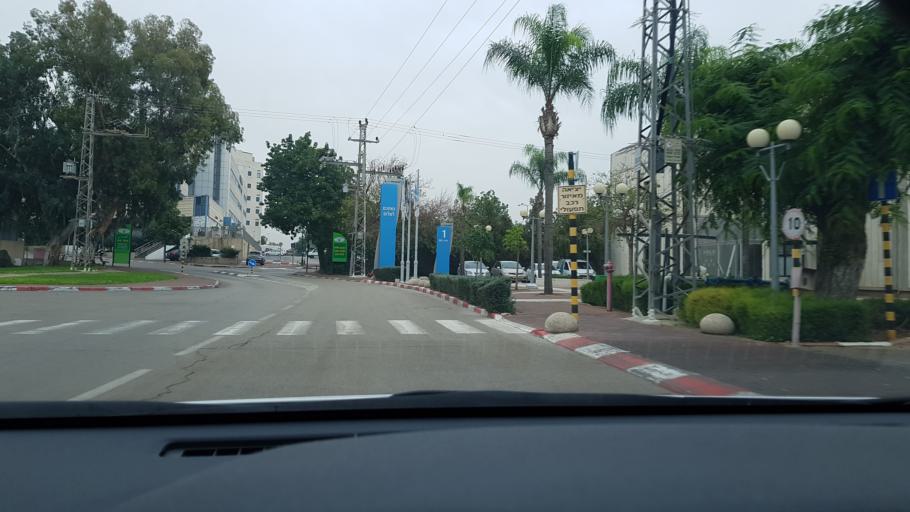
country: IL
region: Central District
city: Ness Ziona
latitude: 31.9143
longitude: 34.8037
